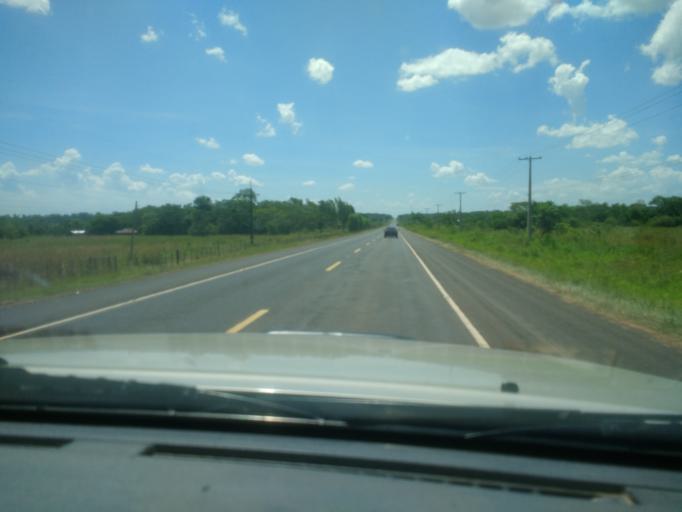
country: PY
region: San Pedro
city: Itacurubi del Rosario
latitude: -24.5090
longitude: -56.8562
